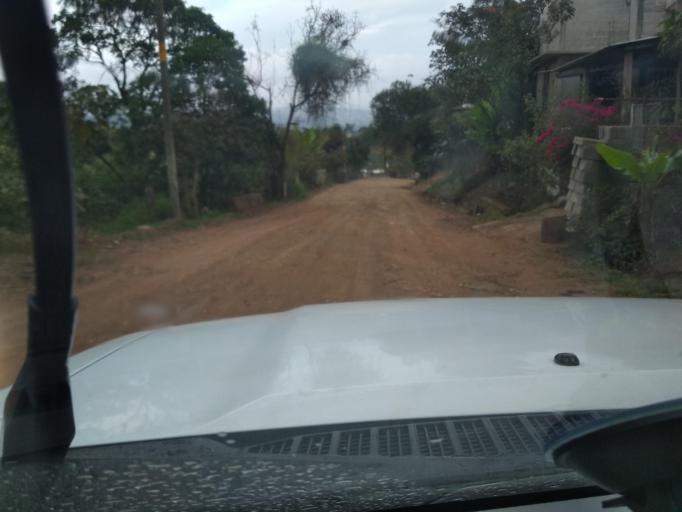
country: MX
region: Veracruz
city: El Castillo
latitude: 19.5394
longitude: -96.8299
